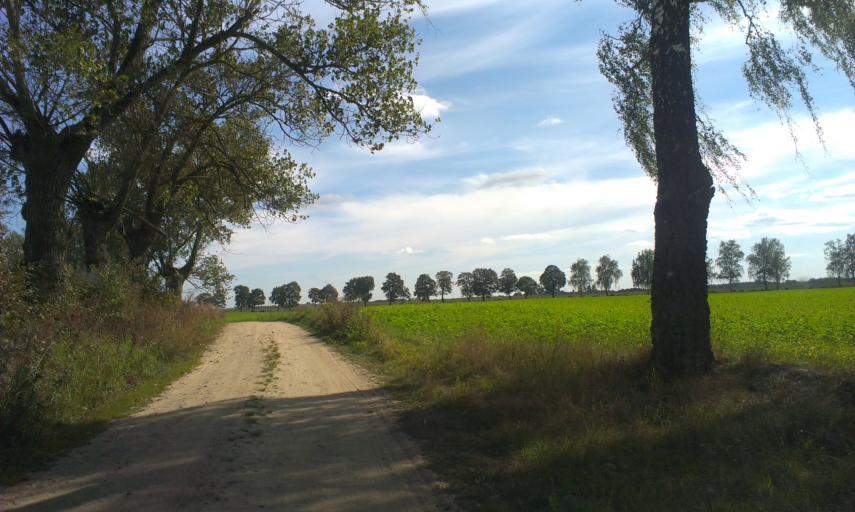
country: PL
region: Greater Poland Voivodeship
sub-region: Powiat pilski
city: Lobzenica
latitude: 53.2857
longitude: 17.1716
